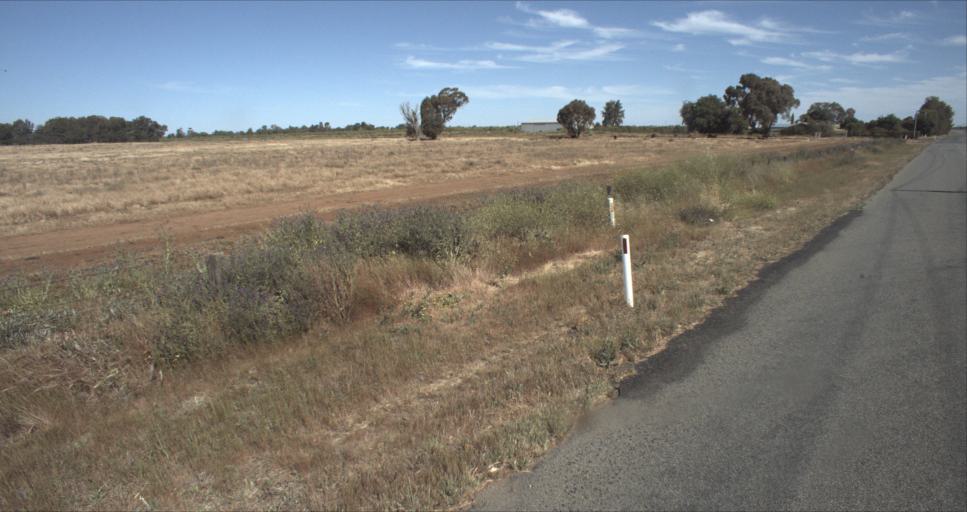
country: AU
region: New South Wales
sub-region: Leeton
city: Leeton
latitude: -34.5627
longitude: 146.3833
